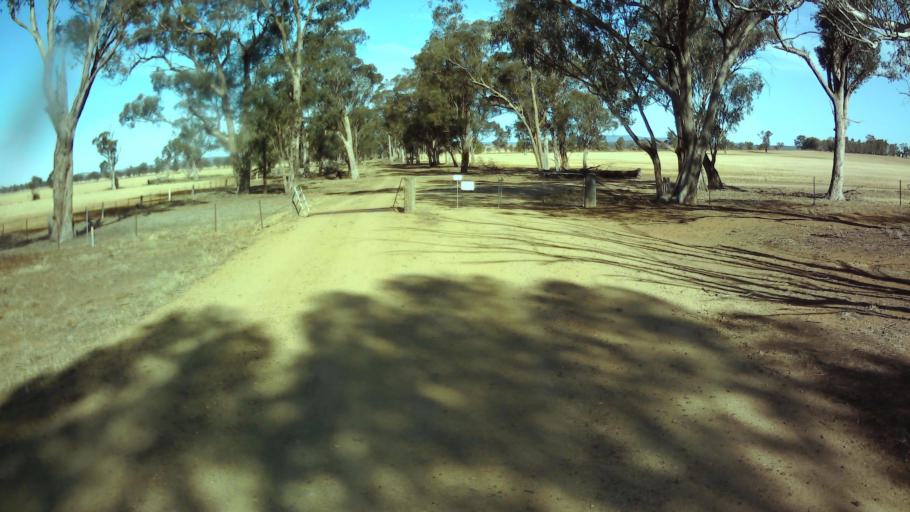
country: AU
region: New South Wales
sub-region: Weddin
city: Grenfell
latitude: -33.6609
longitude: 148.1214
